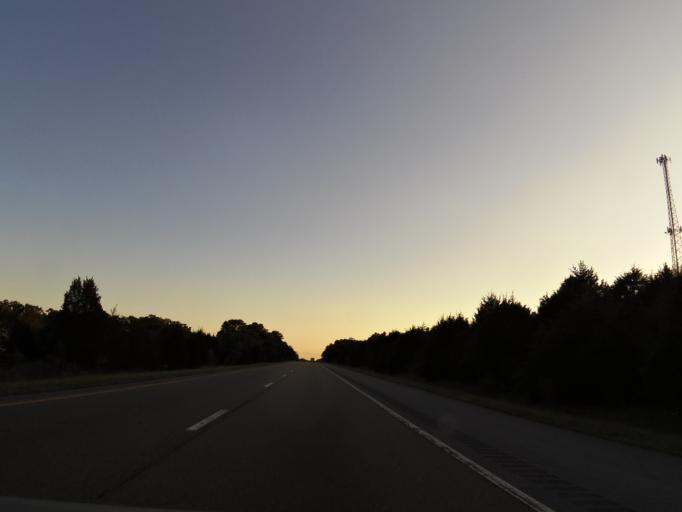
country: US
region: Tennessee
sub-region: Greene County
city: Mosheim
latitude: 36.2954
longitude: -82.8858
